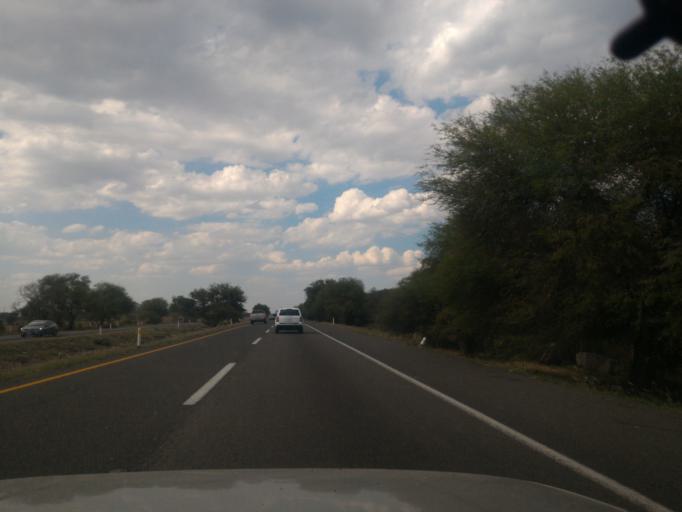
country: MX
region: Jalisco
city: Zacoalco de Torres
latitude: 20.2058
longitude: -103.5269
